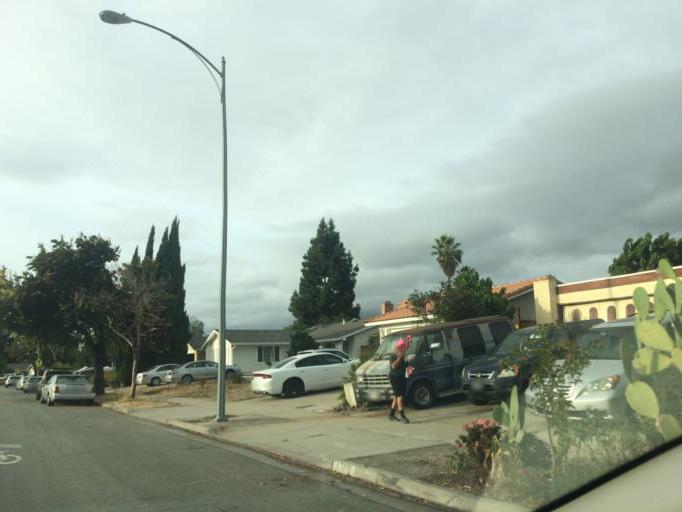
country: US
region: California
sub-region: Santa Clara County
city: Milpitas
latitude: 37.3924
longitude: -121.8807
